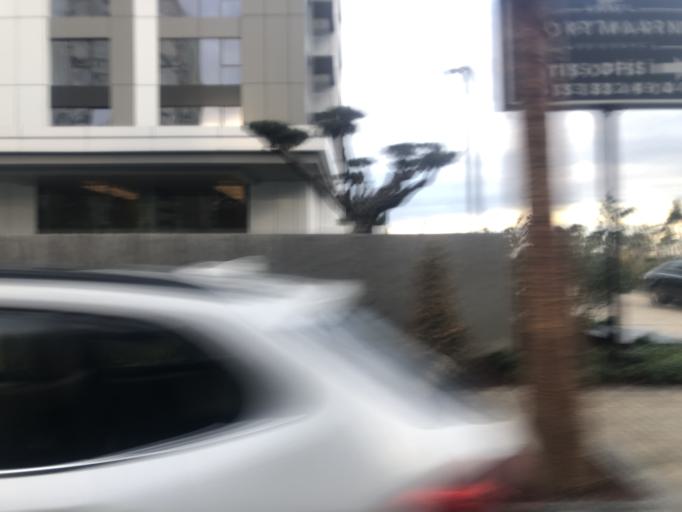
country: TR
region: Izmir
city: Karsiyaka
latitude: 38.4698
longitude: 27.0663
